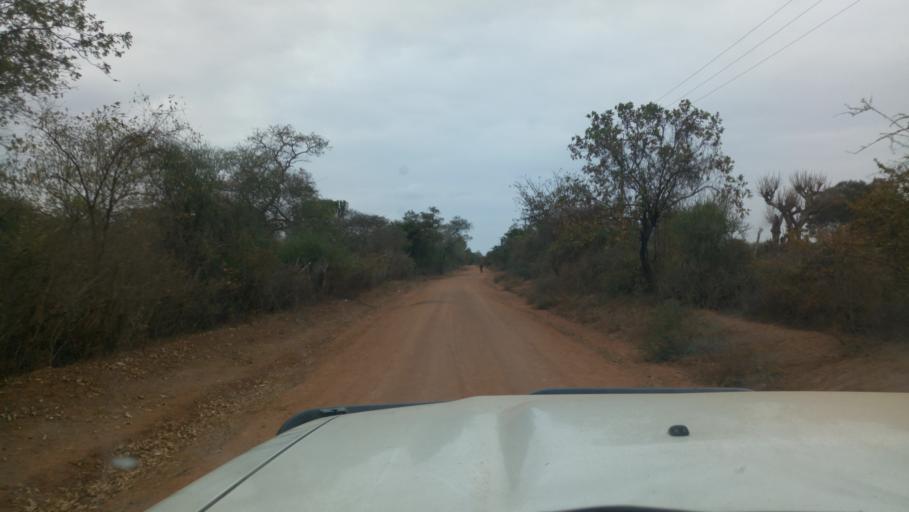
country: KE
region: Kitui
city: Kitui
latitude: -1.8625
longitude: 38.1911
